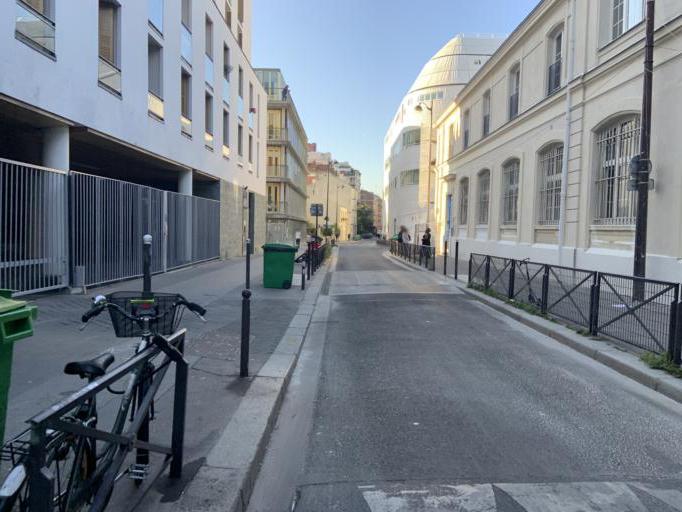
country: FR
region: Ile-de-France
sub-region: Departement du Val-de-Marne
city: Saint-Mande
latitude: 48.8511
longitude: 2.4073
